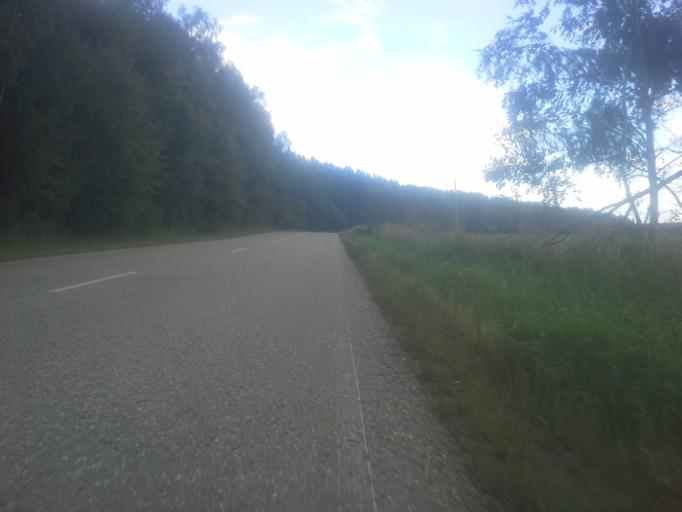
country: RU
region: Moskovskaya
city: Kolyubakino
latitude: 55.6532
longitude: 36.6017
